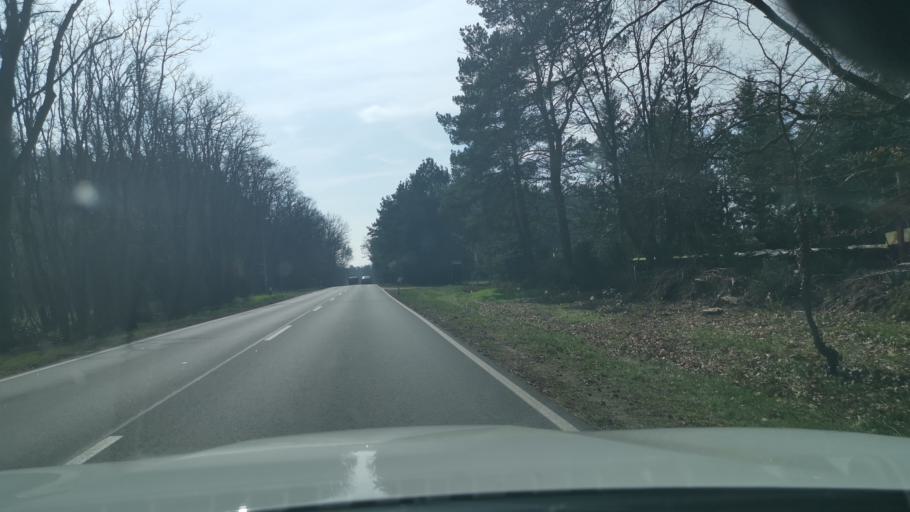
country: DE
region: Saxony
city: Bad Duben
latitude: 51.6103
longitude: 12.5871
